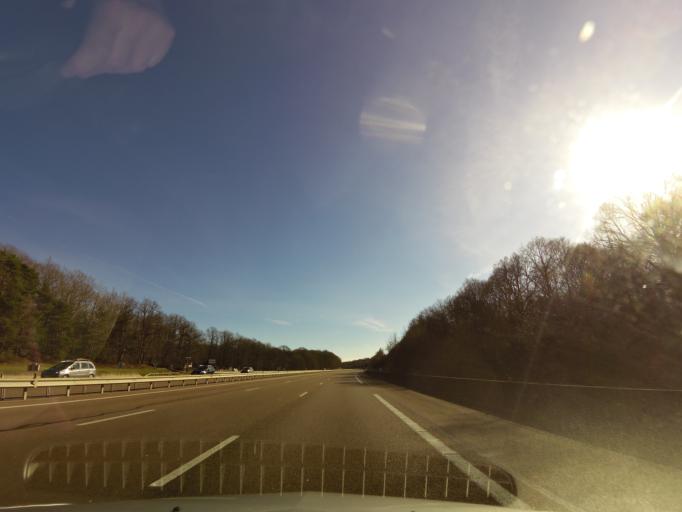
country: FR
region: Bourgogne
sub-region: Departement de l'Yonne
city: Aillant-sur-Tholon
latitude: 47.9200
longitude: 3.2854
